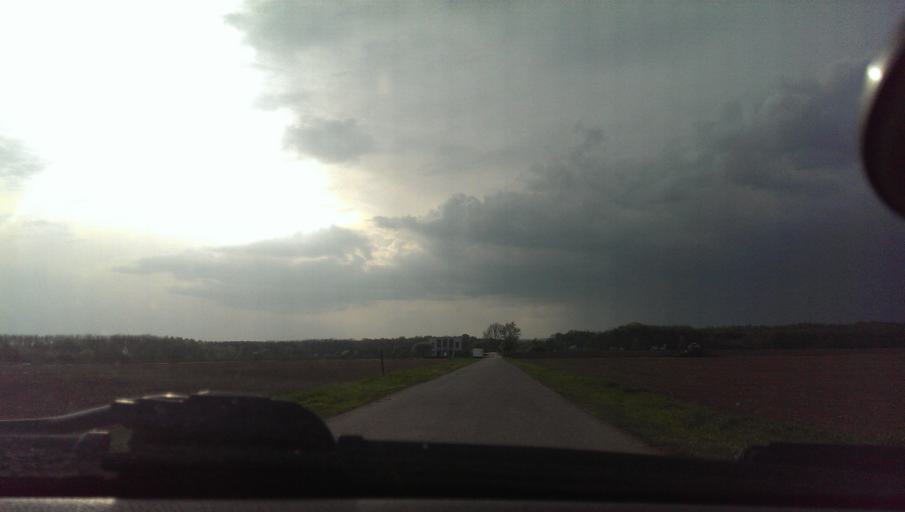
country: CZ
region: Zlin
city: Knezpole
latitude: 49.1033
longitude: 17.5094
